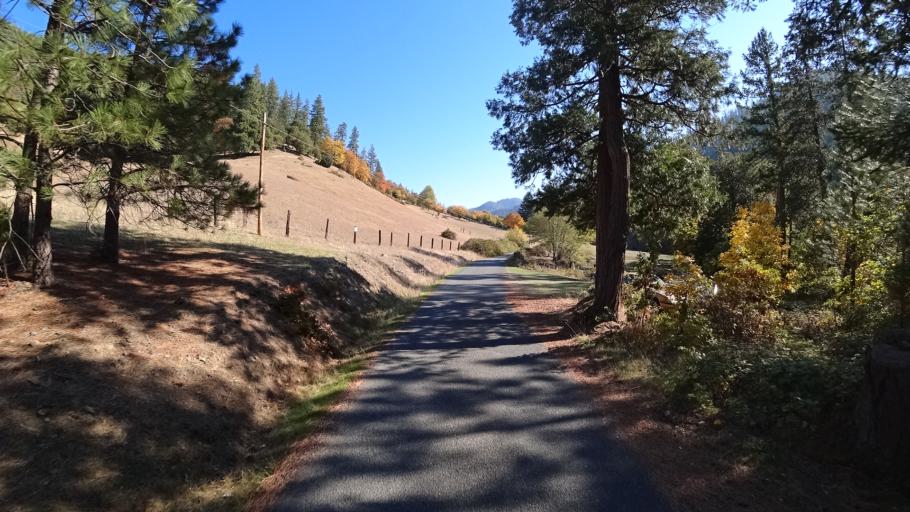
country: US
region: California
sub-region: Siskiyou County
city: Yreka
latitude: 41.7422
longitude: -122.9881
